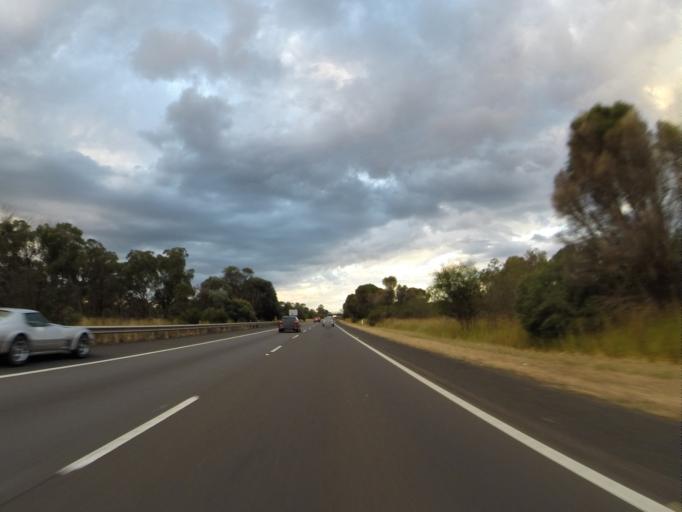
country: AU
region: New South Wales
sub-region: Wollondilly
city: Douglas Park
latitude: -34.1860
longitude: 150.7175
